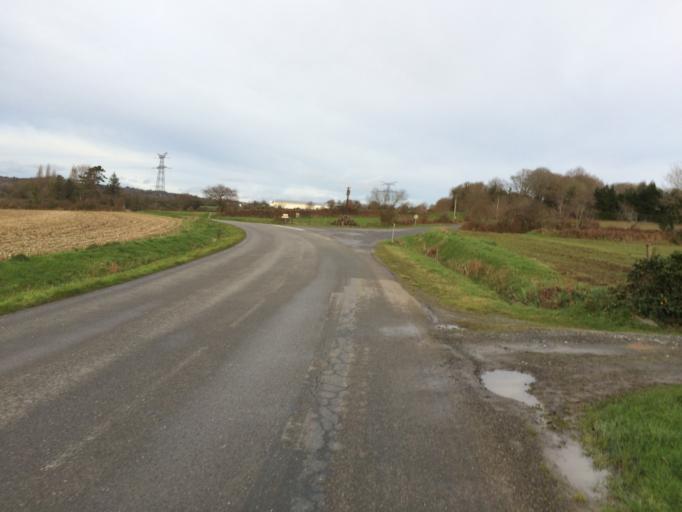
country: FR
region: Brittany
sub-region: Departement du Finistere
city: Saint-Urbain
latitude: 48.3844
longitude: -4.2367
